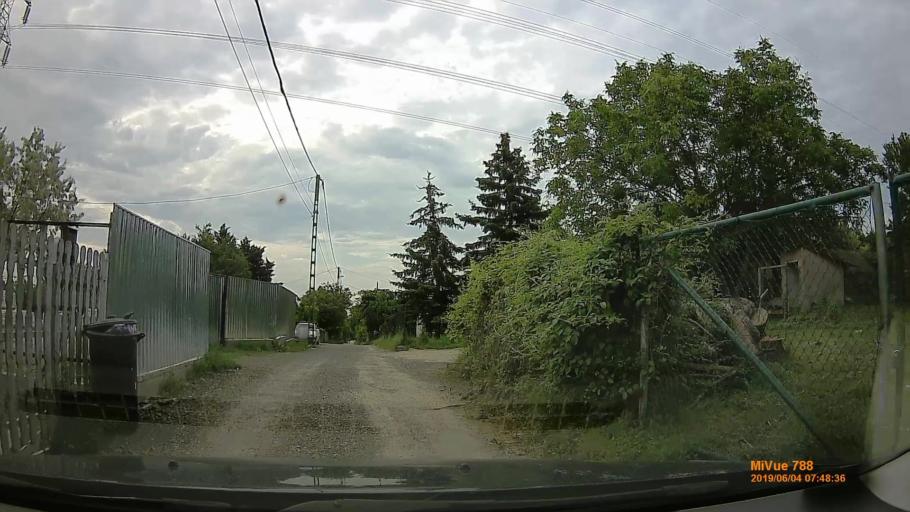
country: HU
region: Pest
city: Diosd
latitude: 47.4164
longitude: 18.9841
